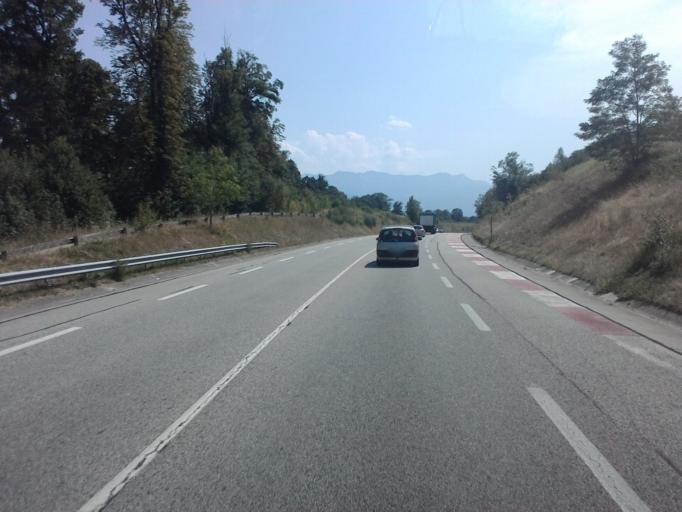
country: FR
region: Rhone-Alpes
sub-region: Departement de l'Isere
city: Voiron
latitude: 45.3850
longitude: 5.5747
